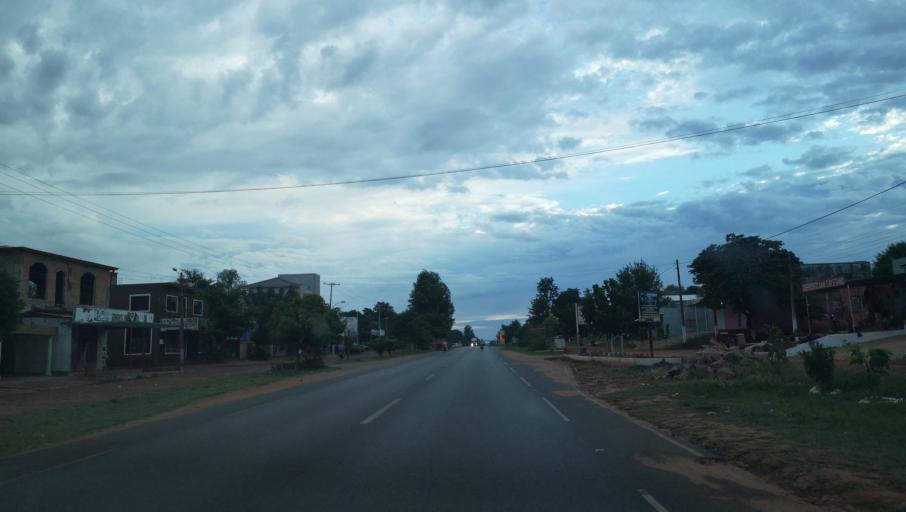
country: PY
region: San Pedro
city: Capiibary
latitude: -24.7224
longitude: -56.0162
